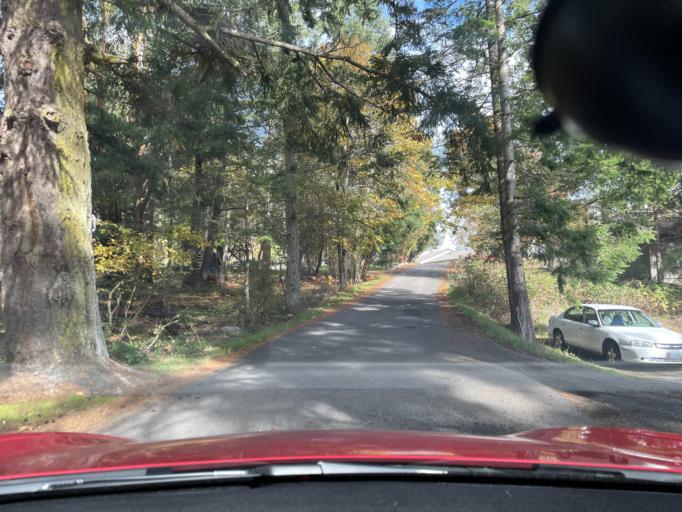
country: US
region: Washington
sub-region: San Juan County
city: Friday Harbor
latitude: 48.5307
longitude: -123.0286
